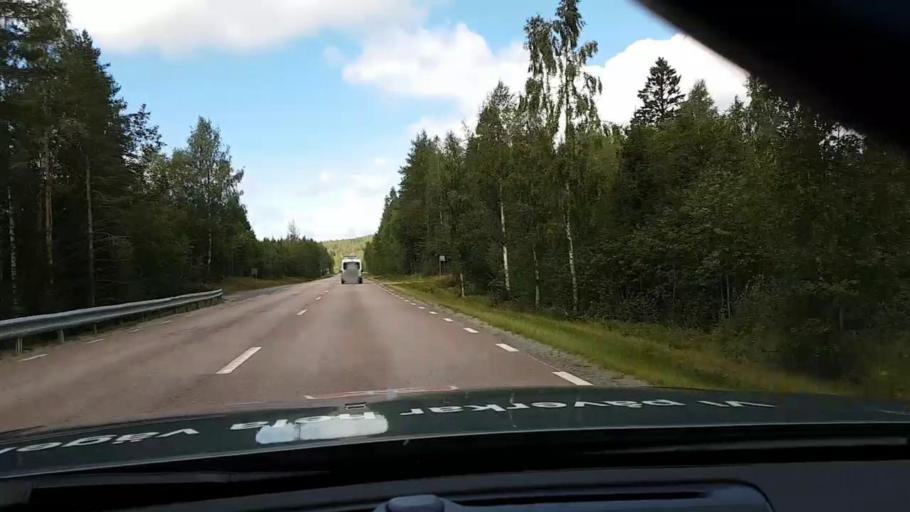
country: SE
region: Vaesternorrland
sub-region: OErnskoeldsviks Kommun
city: Bjasta
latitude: 63.3750
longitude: 18.4299
